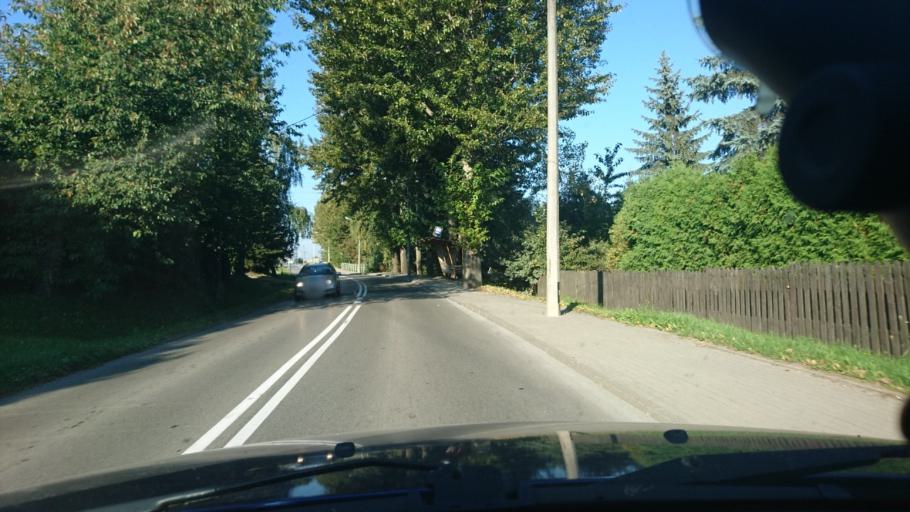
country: PL
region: Silesian Voivodeship
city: Janowice
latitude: 49.8512
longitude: 19.0778
